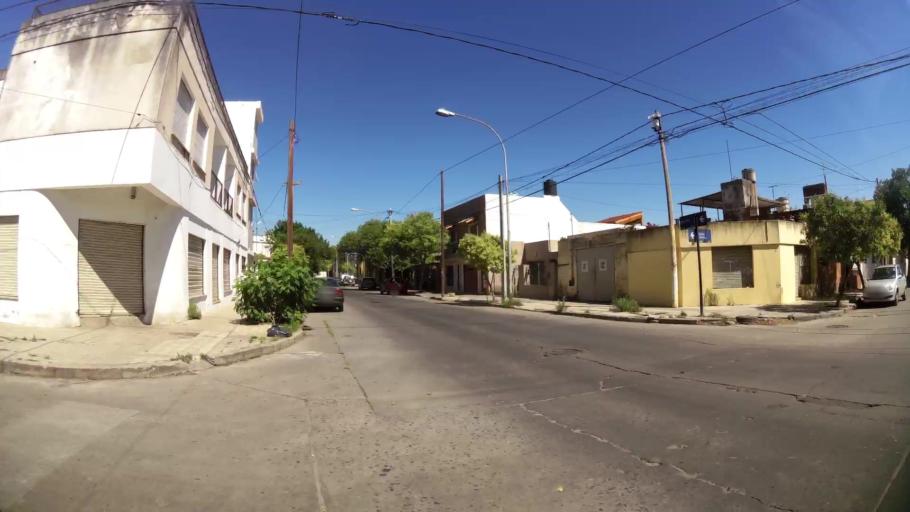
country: AR
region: Cordoba
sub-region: Departamento de Capital
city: Cordoba
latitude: -31.4236
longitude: -64.1595
